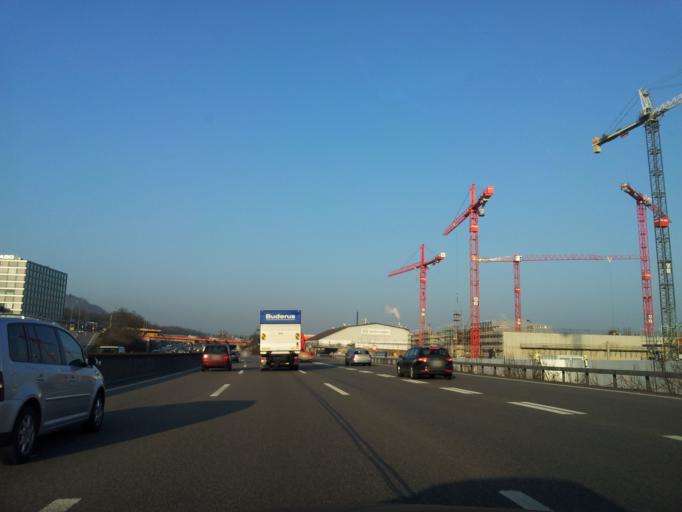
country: CH
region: Basel-Landschaft
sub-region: Bezirk Liestal
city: Pratteln
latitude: 47.5291
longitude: 7.6911
